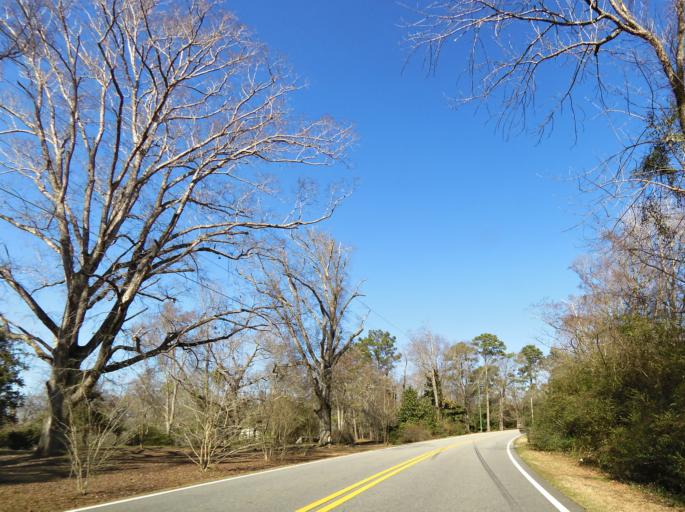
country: US
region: Georgia
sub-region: Bibb County
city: West Point
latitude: 32.8390
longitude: -83.8096
